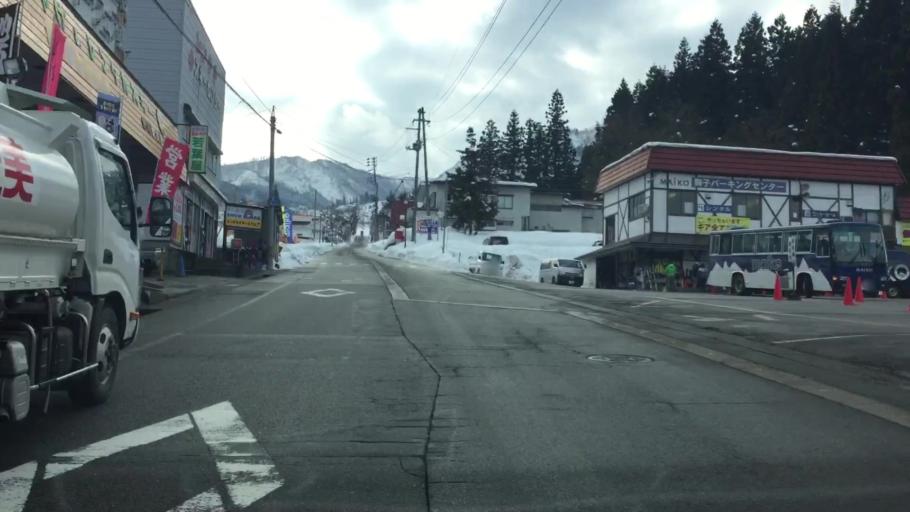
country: JP
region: Niigata
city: Shiozawa
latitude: 36.9874
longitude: 138.8222
